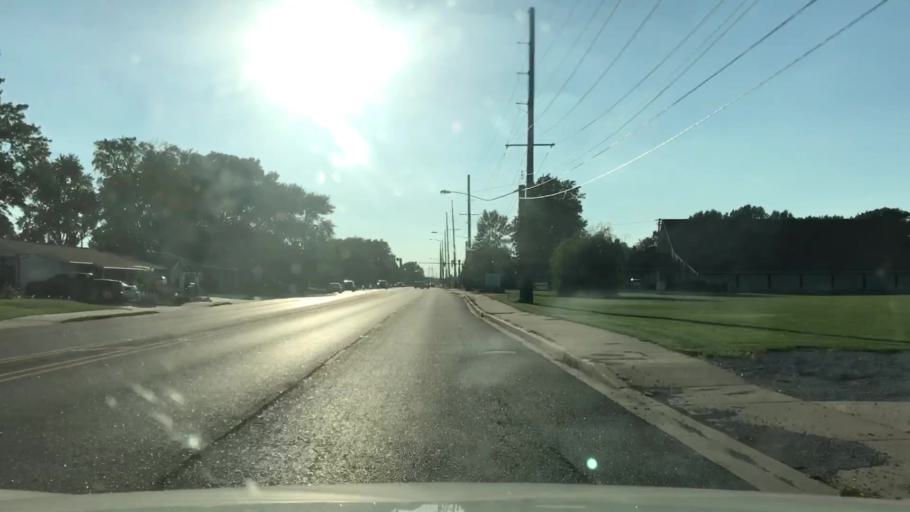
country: US
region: Illinois
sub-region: Madison County
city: Granite City
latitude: 38.7316
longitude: -90.1287
